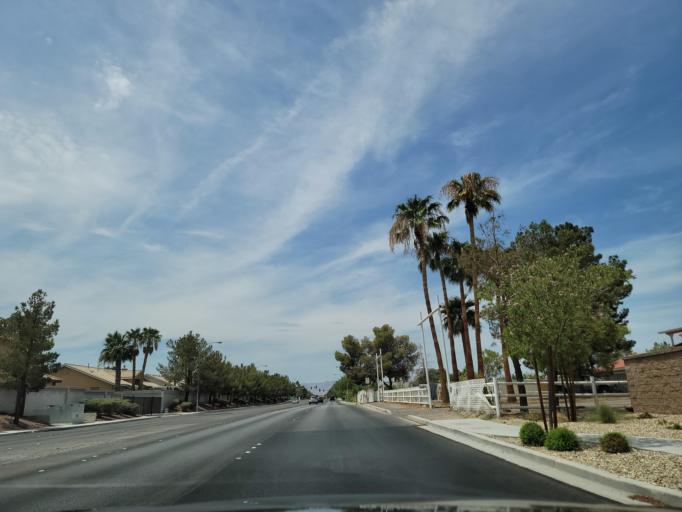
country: US
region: Nevada
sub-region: Clark County
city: Whitney
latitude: 36.0207
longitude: -115.1328
